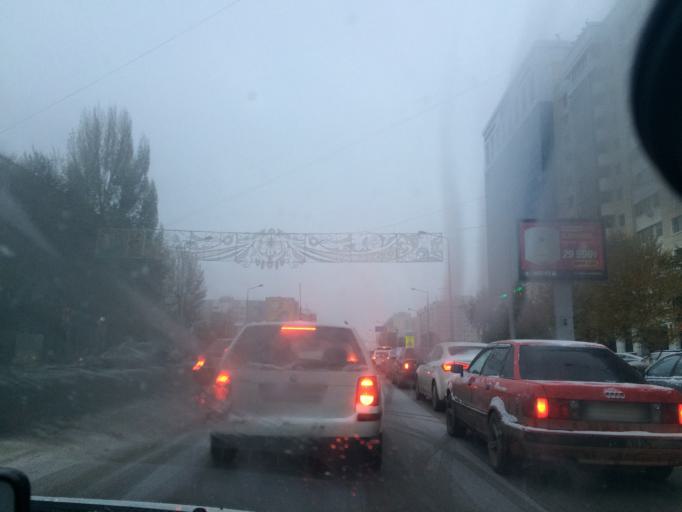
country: KZ
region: Astana Qalasy
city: Astana
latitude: 51.1678
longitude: 71.4083
